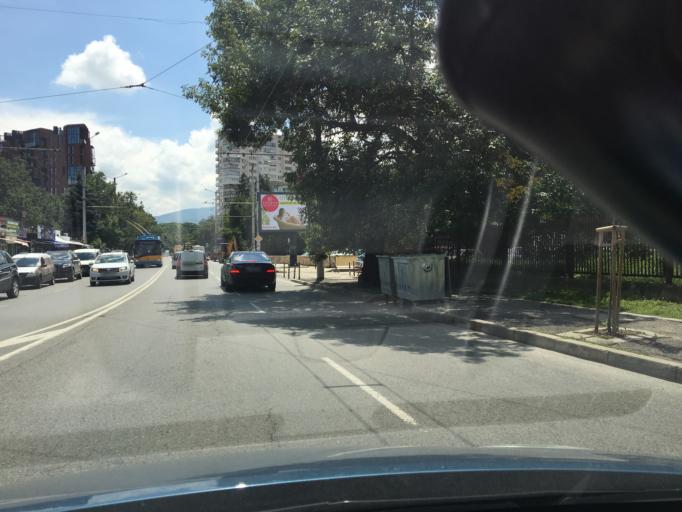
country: BG
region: Sofia-Capital
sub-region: Stolichna Obshtina
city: Sofia
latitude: 42.6769
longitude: 23.3031
